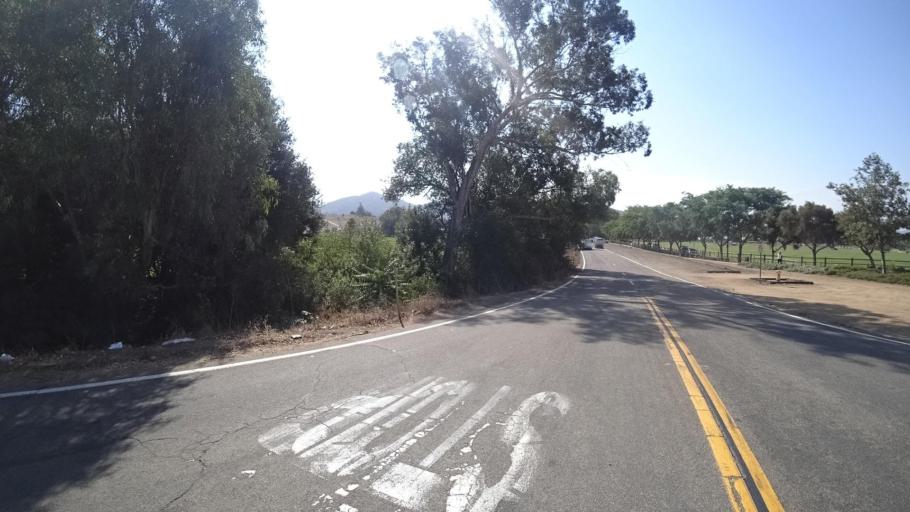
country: US
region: California
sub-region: San Diego County
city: San Marcos
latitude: 33.1863
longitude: -117.1520
